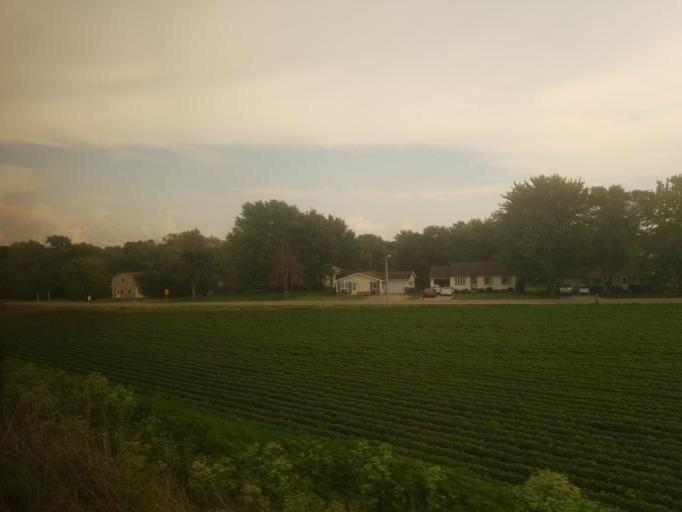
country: US
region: Illinois
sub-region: Bureau County
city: Princeton
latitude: 41.3867
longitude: -89.4764
